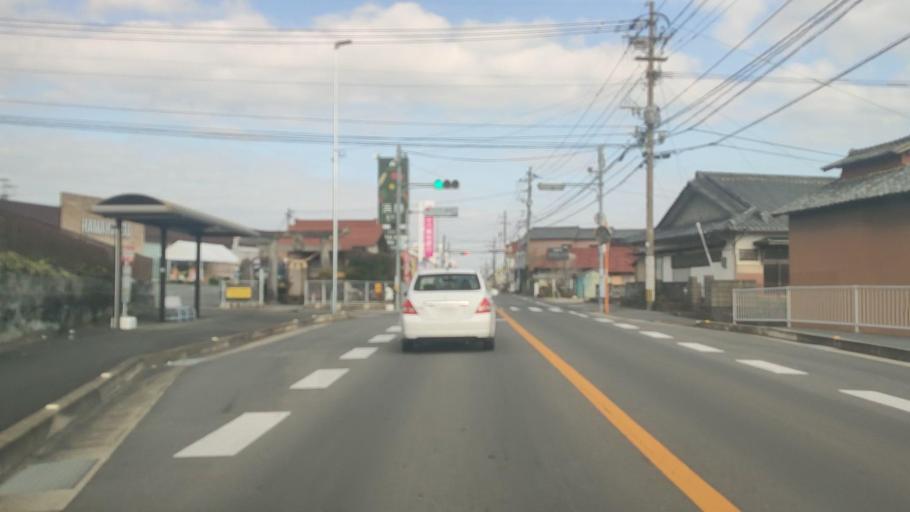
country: JP
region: Nagasaki
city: Shimabara
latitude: 32.7158
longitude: 130.3494
